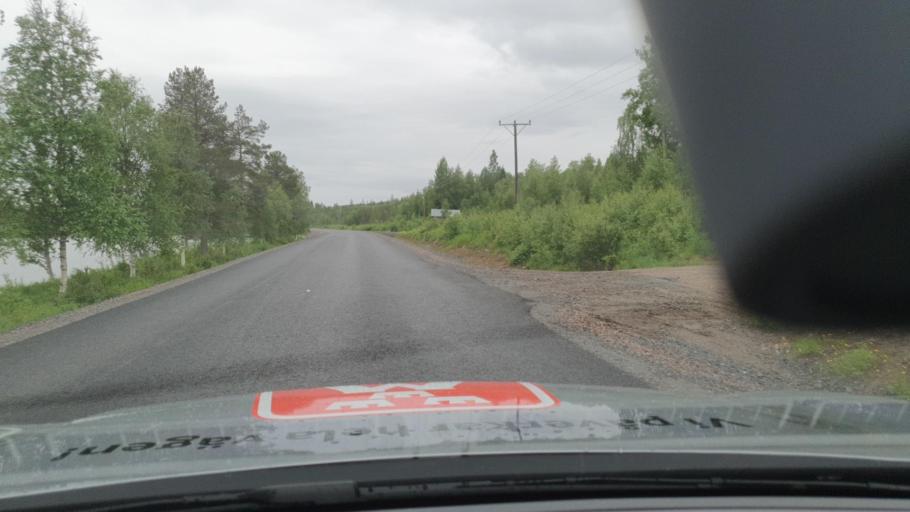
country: SE
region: Norrbotten
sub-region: Pajala Kommun
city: Pajala
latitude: 66.7400
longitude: 23.1694
